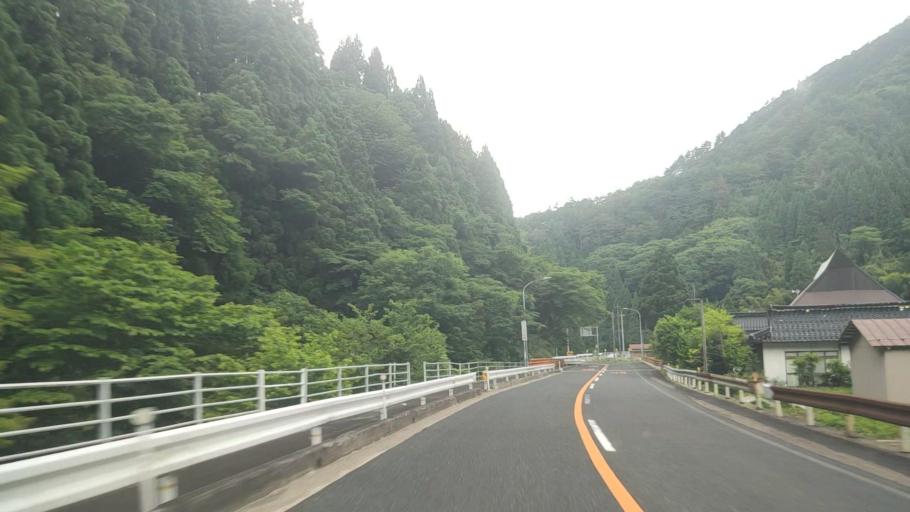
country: JP
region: Tottori
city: Kurayoshi
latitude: 35.3167
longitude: 133.8896
